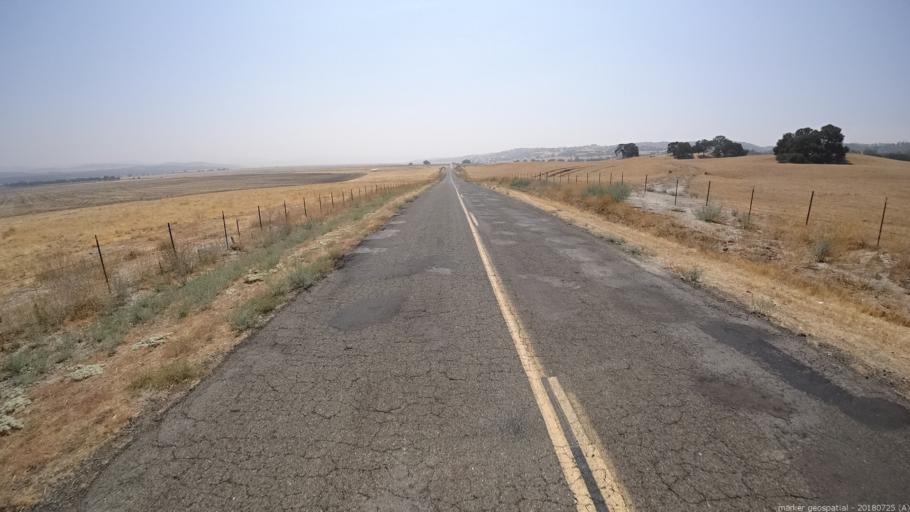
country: US
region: California
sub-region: San Luis Obispo County
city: Shandon
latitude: 35.8074
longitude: -120.3696
